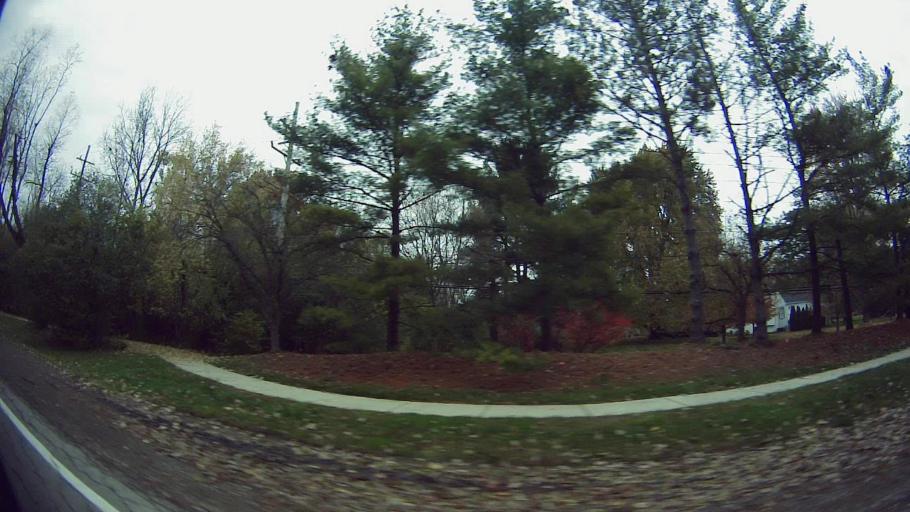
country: US
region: Michigan
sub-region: Oakland County
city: Bingham Farms
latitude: 42.5308
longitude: -83.2515
